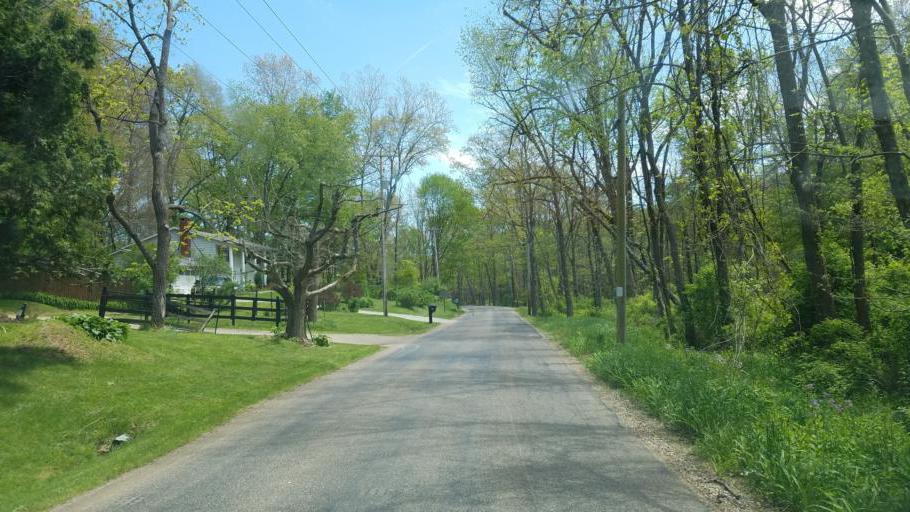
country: US
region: Ohio
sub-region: Knox County
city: Gambier
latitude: 40.3906
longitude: -82.4355
